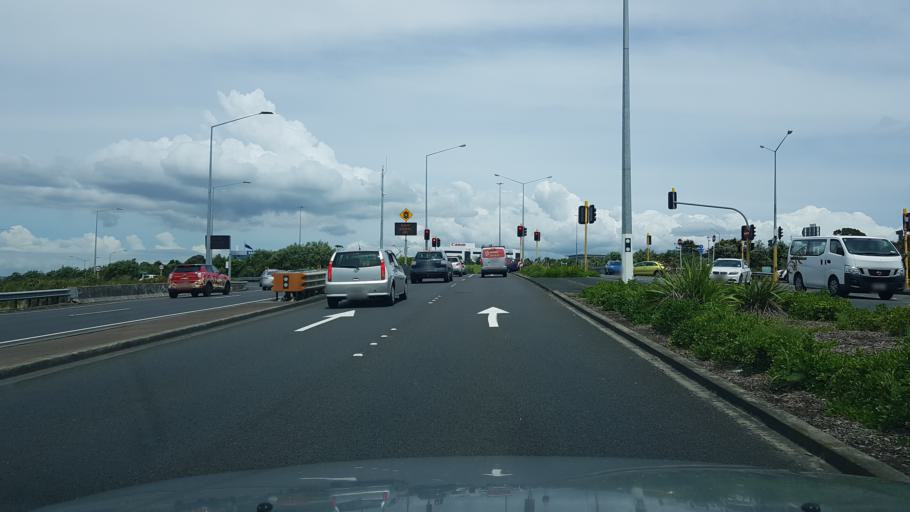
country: NZ
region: Auckland
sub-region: Auckland
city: North Shore
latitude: -36.7987
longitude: 174.7625
